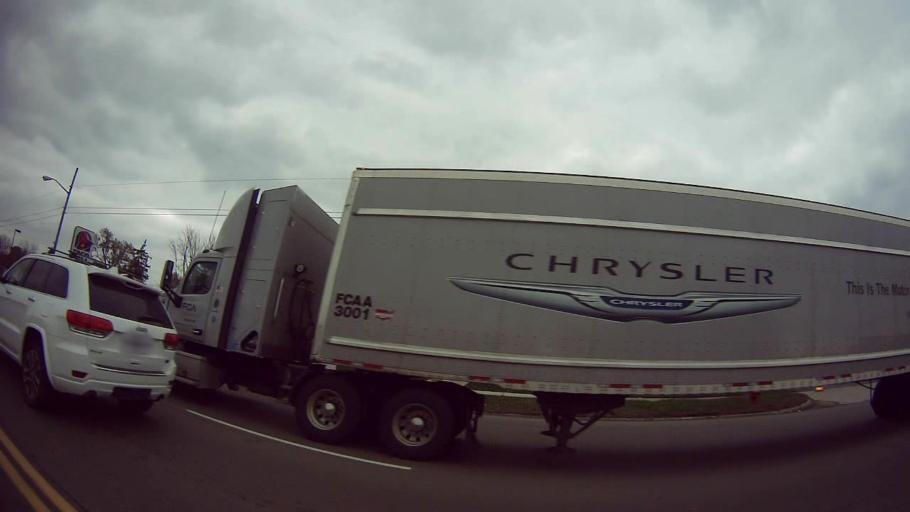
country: US
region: Michigan
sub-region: Macomb County
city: Center Line
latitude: 42.5302
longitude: -83.0292
